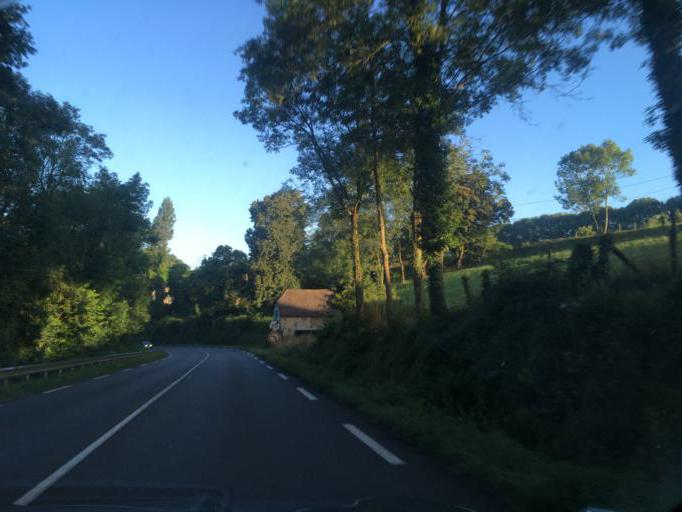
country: FR
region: Aquitaine
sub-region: Departement des Pyrenees-Atlantiques
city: Soumoulou
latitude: 43.2596
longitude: -0.1655
